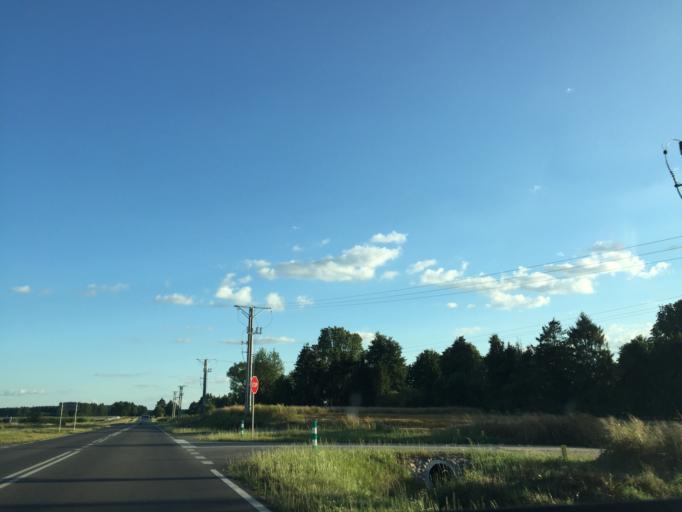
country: PL
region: Podlasie
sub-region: Lomza
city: Lomza
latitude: 53.1374
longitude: 22.0508
